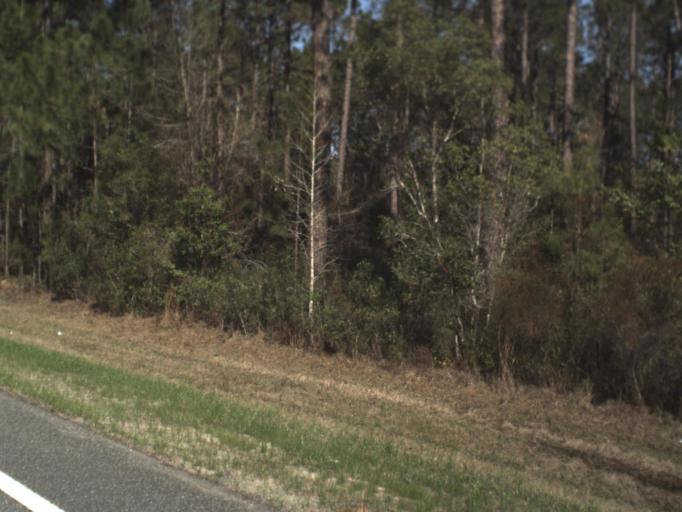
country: US
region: Florida
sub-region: Calhoun County
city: Blountstown
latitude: 30.3865
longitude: -85.0852
